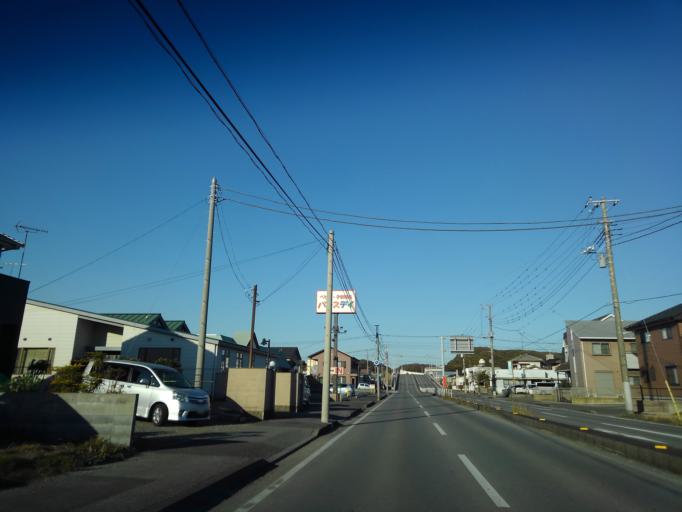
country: JP
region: Chiba
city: Kimitsu
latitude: 35.3327
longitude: 139.8888
